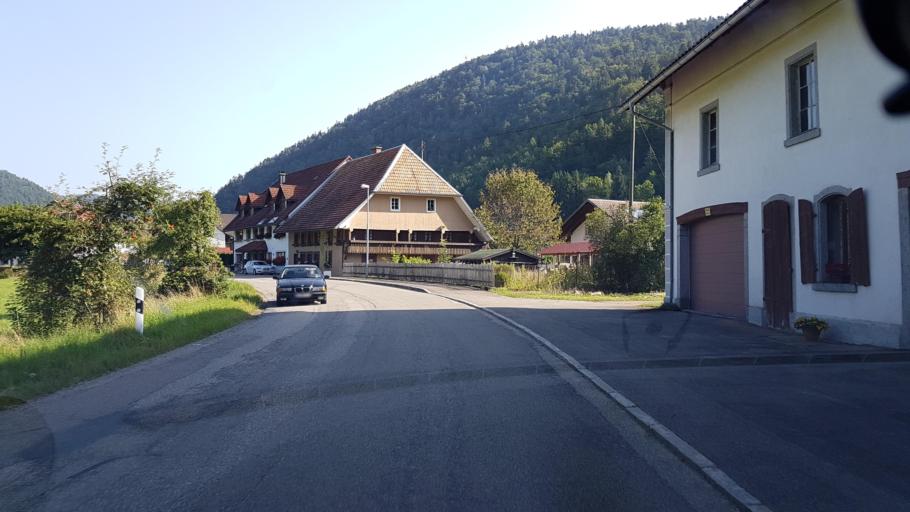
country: DE
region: Baden-Wuerttemberg
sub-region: Freiburg Region
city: Dachsberg
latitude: 47.6944
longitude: 8.1246
